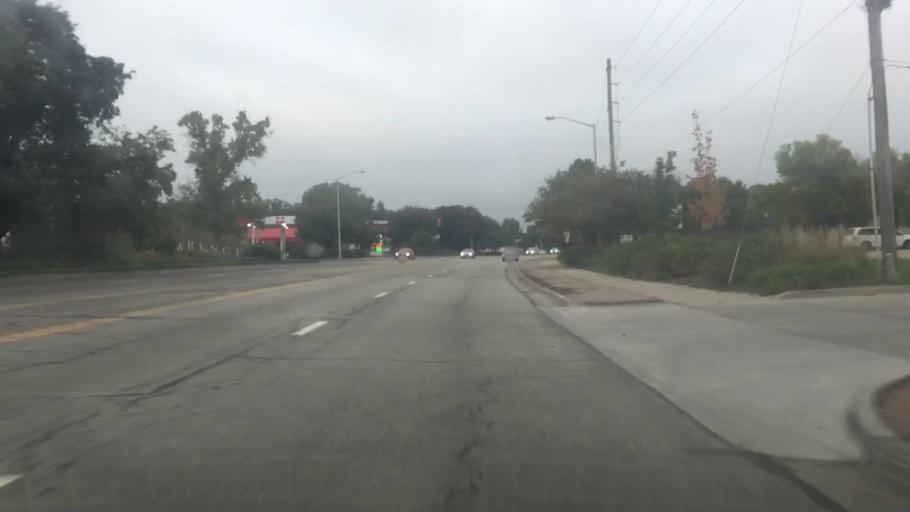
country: US
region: Kansas
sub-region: Douglas County
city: Lawrence
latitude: 38.9880
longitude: -95.2336
